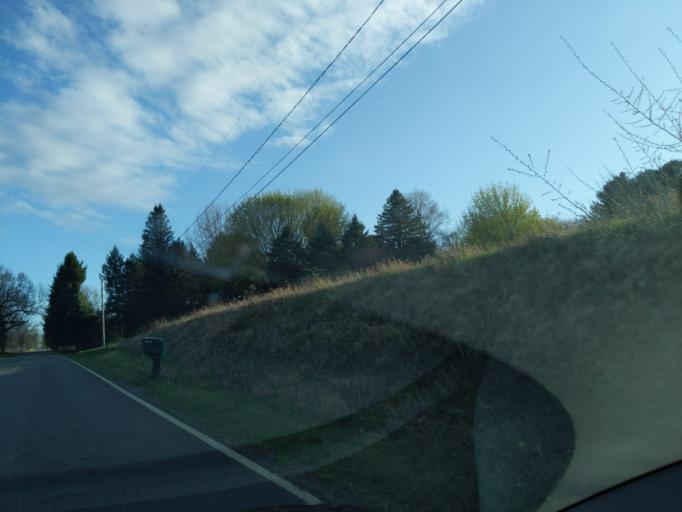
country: US
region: Michigan
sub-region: Ingham County
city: Leslie
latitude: 42.3768
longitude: -84.4625
